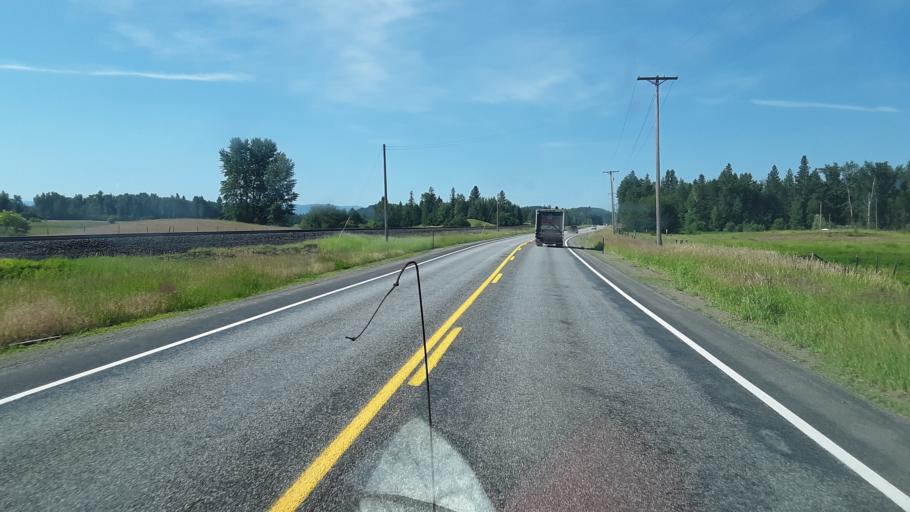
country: US
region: Idaho
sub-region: Bonner County
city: Ponderay
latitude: 48.4544
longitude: -116.4766
